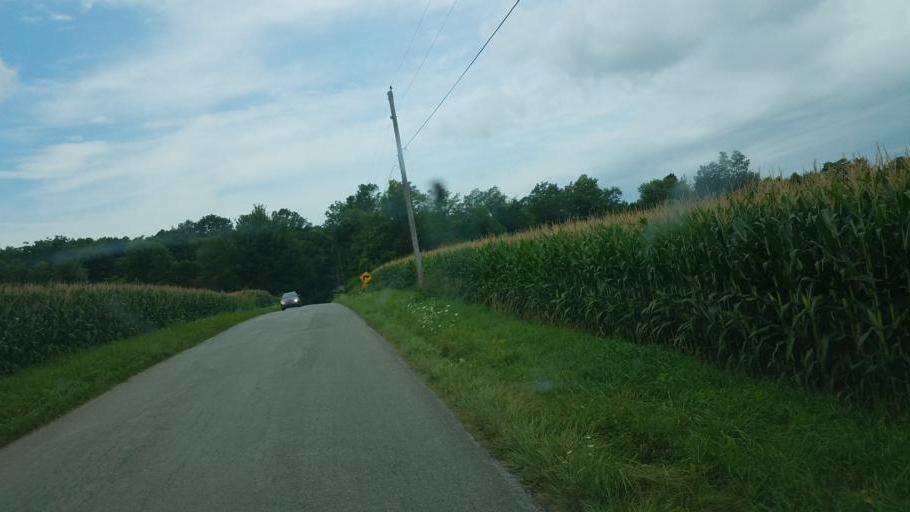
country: US
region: Pennsylvania
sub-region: Erie County
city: Lake City
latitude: 42.0019
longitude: -80.4360
